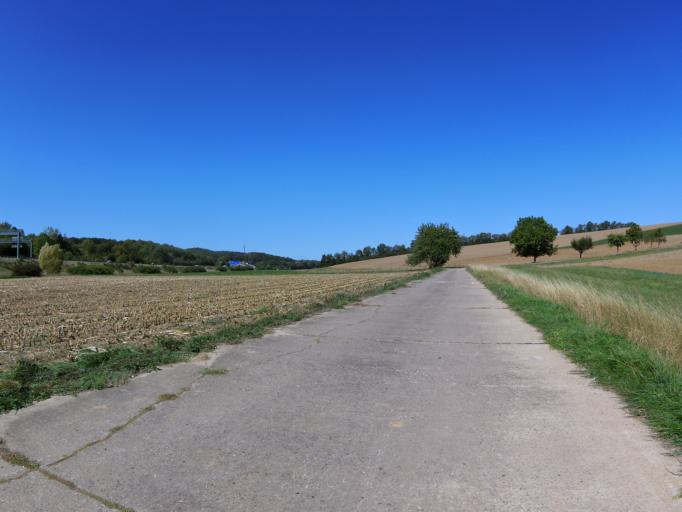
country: DE
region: Bavaria
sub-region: Regierungsbezirk Unterfranken
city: Waldbrunn
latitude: 49.7584
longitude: 9.7851
